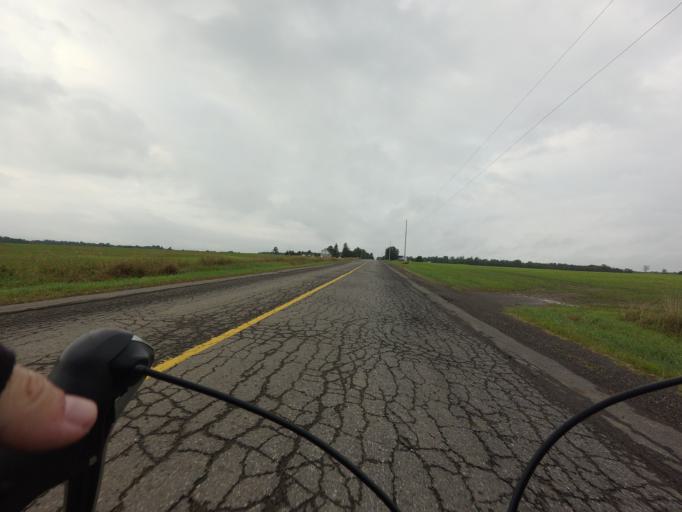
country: CA
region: Ontario
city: Bells Corners
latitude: 45.1191
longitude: -75.7754
